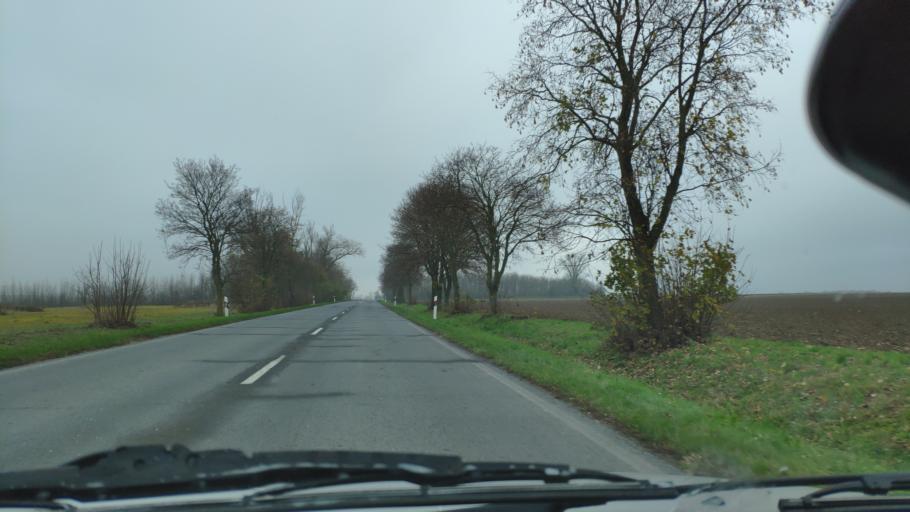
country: HU
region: Zala
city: Zalakomar
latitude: 46.5778
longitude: 17.2634
